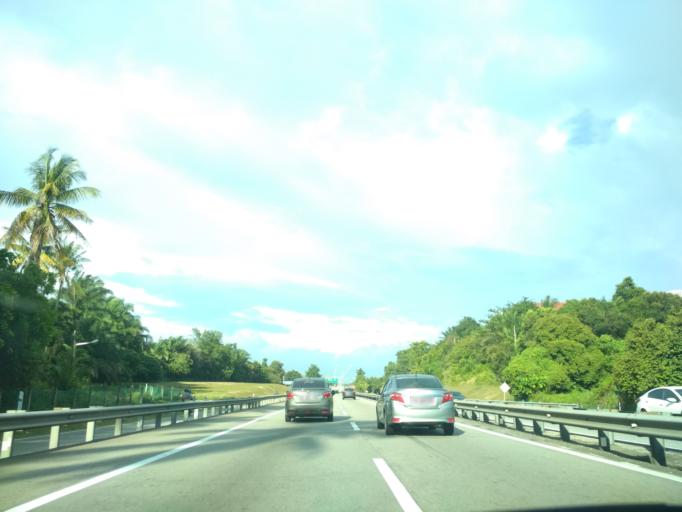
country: MY
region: Penang
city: Bukit Mertajam
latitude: 5.4043
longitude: 100.4803
